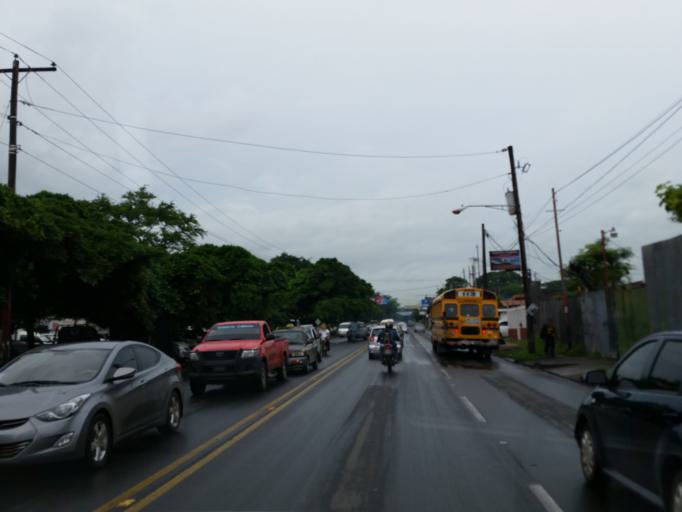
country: NI
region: Managua
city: Managua
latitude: 12.1440
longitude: -86.2920
